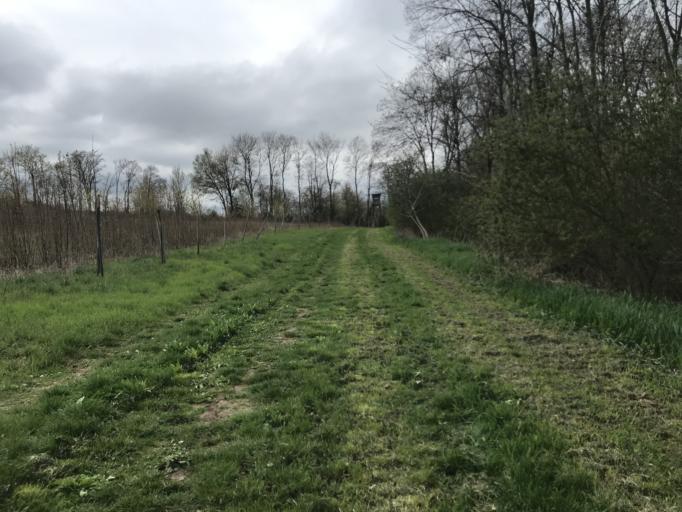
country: DE
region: Rheinland-Pfalz
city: Schwabenheim
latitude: 49.9360
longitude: 8.1100
